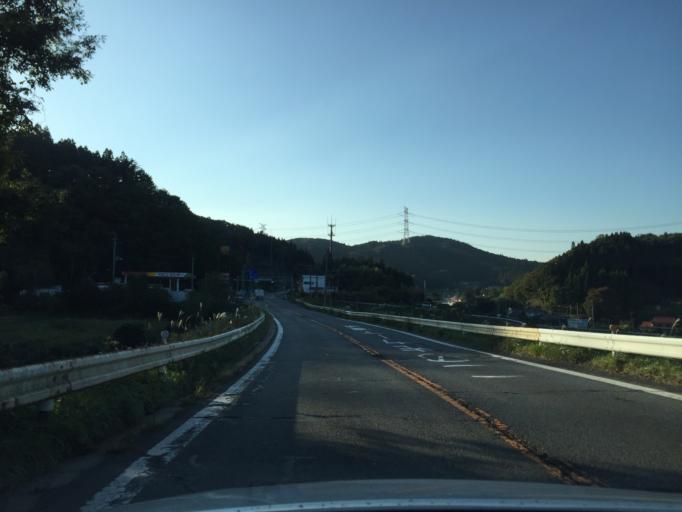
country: JP
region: Fukushima
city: Ishikawa
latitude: 37.1919
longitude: 140.6356
